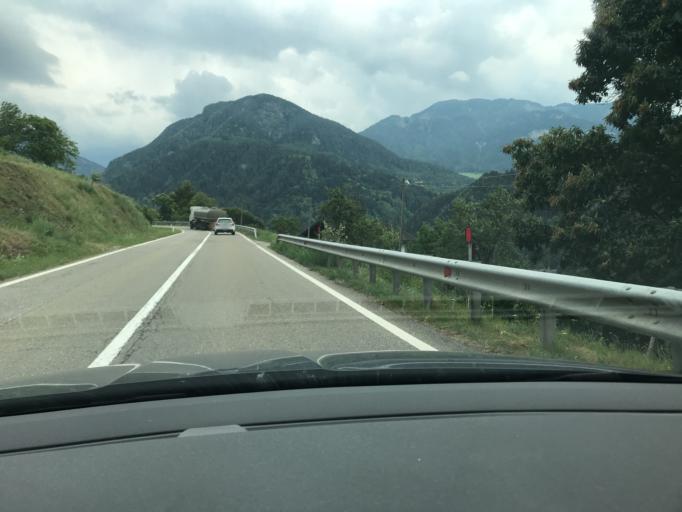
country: IT
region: Trentino-Alto Adige
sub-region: Bolzano
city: Laion
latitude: 46.5992
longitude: 11.5715
